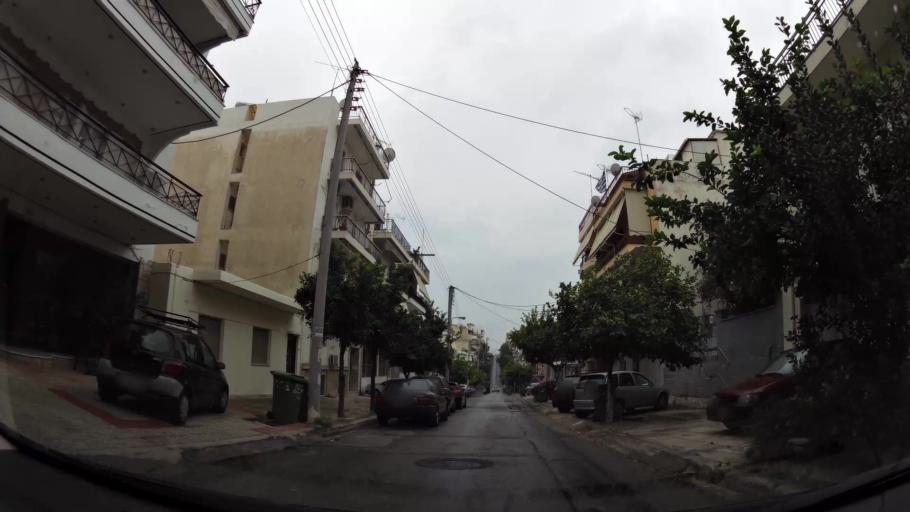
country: GR
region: Attica
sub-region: Nomos Piraios
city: Korydallos
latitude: 37.9901
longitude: 23.6488
